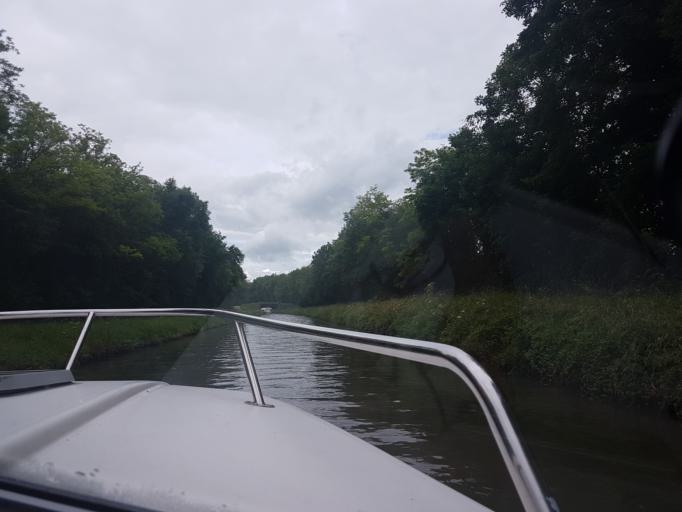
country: FR
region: Bourgogne
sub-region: Departement de l'Yonne
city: Vermenton
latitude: 47.6491
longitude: 3.6672
